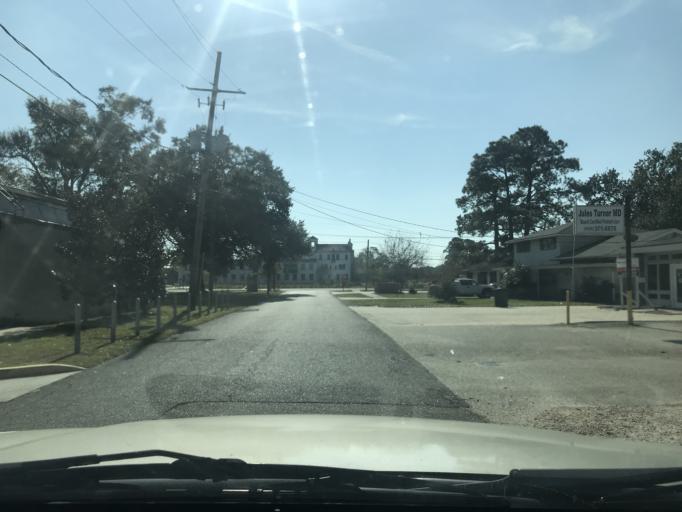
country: US
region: Louisiana
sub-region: Jefferson Parish
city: Marrero
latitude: 29.8939
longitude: -90.0991
